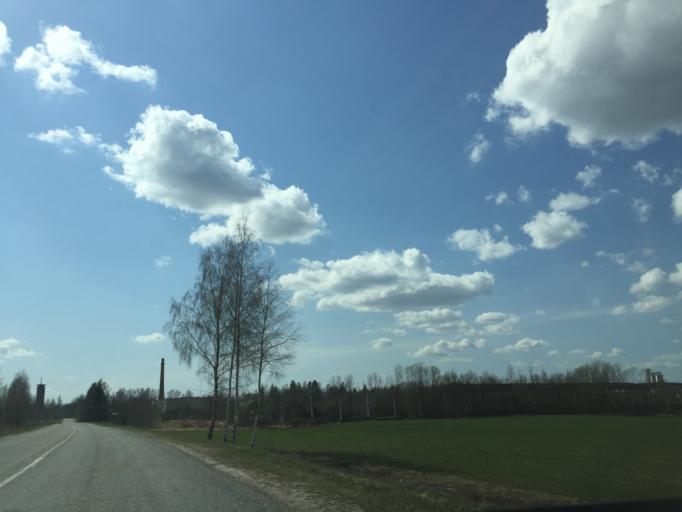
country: LV
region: Ogre
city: Jumprava
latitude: 56.7740
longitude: 25.0036
